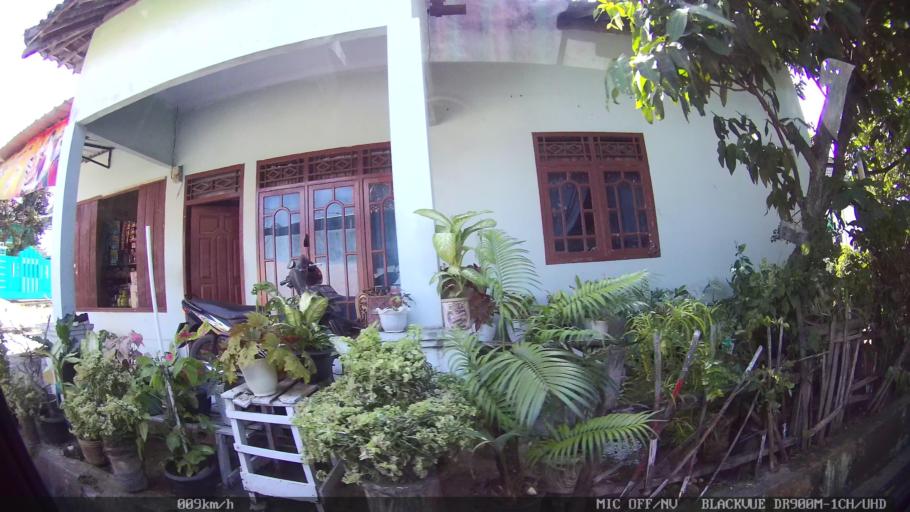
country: ID
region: Lampung
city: Kedaton
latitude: -5.3684
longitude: 105.2525
